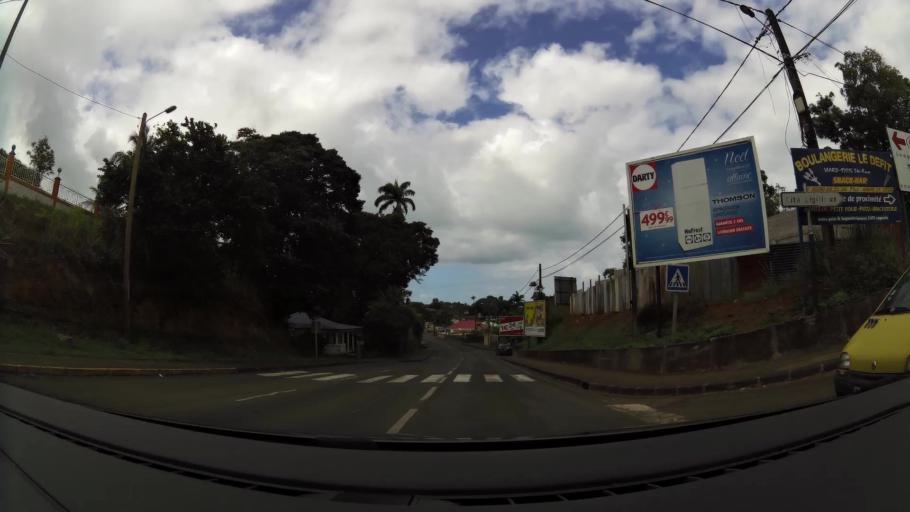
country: GP
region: Guadeloupe
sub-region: Guadeloupe
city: Sainte-Rose
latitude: 16.3188
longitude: -61.6860
